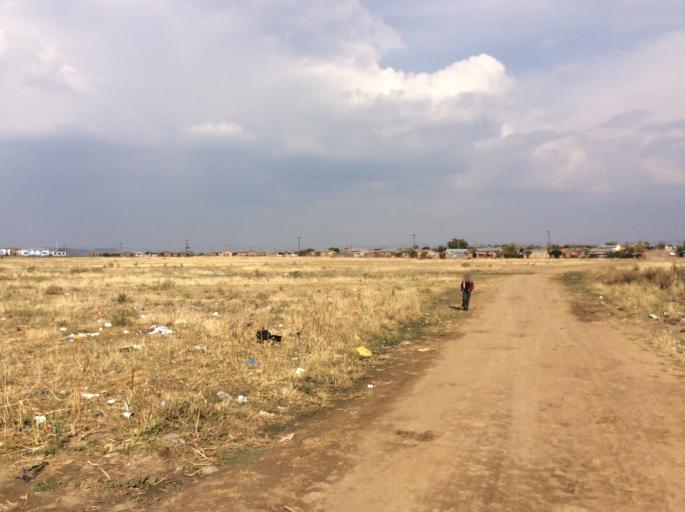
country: LS
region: Mafeteng
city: Mafeteng
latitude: -29.7123
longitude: 27.0114
